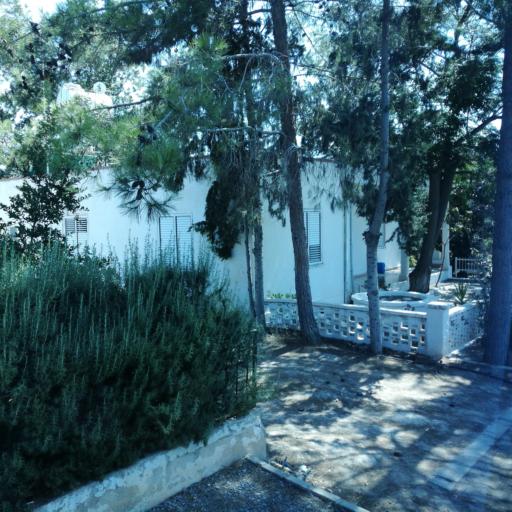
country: CY
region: Ammochostos
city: Acheritou
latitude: 35.0964
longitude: 33.9024
